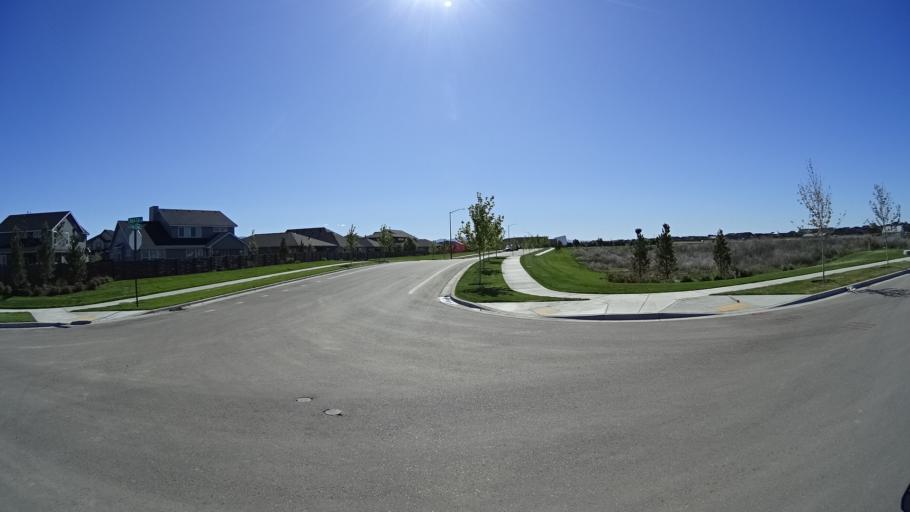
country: US
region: Idaho
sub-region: Ada County
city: Star
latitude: 43.6657
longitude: -116.4534
